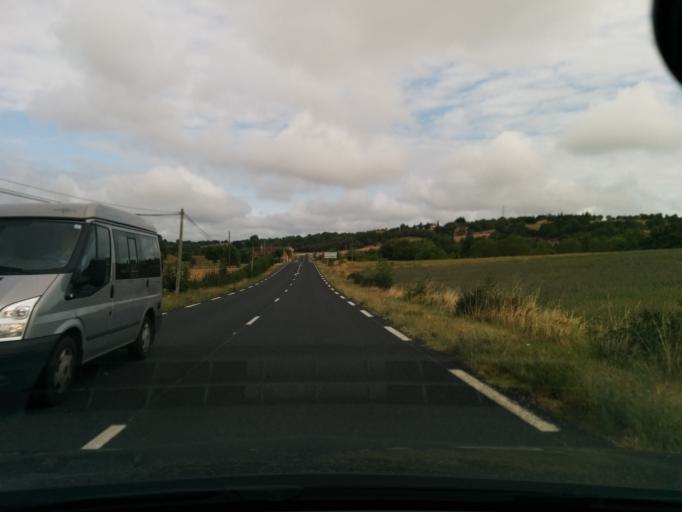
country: FR
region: Midi-Pyrenees
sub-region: Departement du Lot
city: Le Vigan
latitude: 44.7443
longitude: 1.5002
